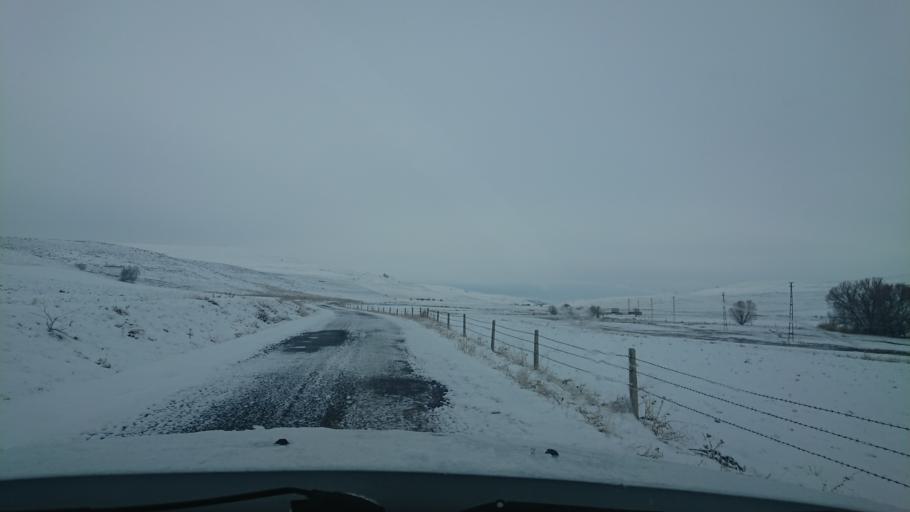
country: TR
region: Aksaray
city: Acipinar
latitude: 38.6800
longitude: 33.8653
